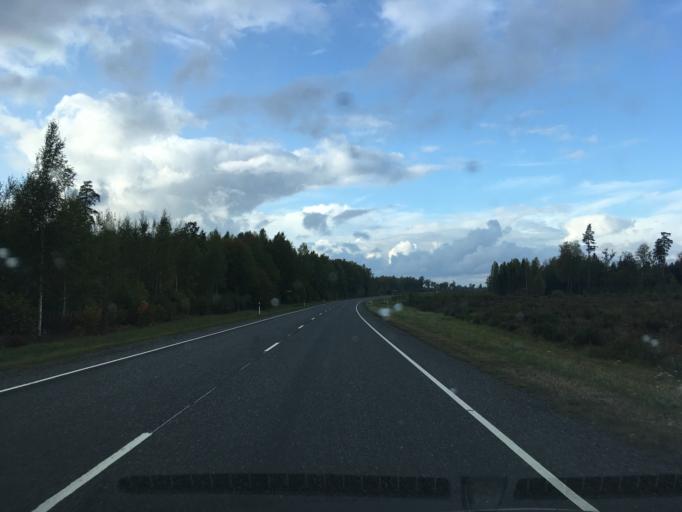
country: EE
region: Harju
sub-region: Nissi vald
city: Turba
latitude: 58.9707
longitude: 24.0638
